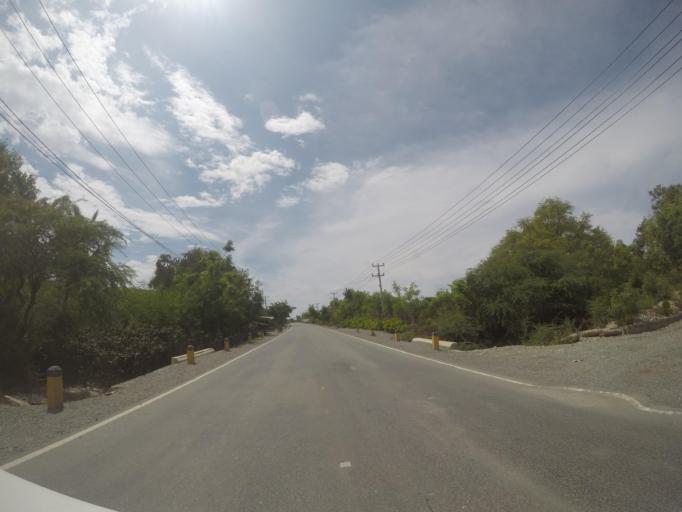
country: TL
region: Liquica
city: Liquica
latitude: -8.5644
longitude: 125.4152
